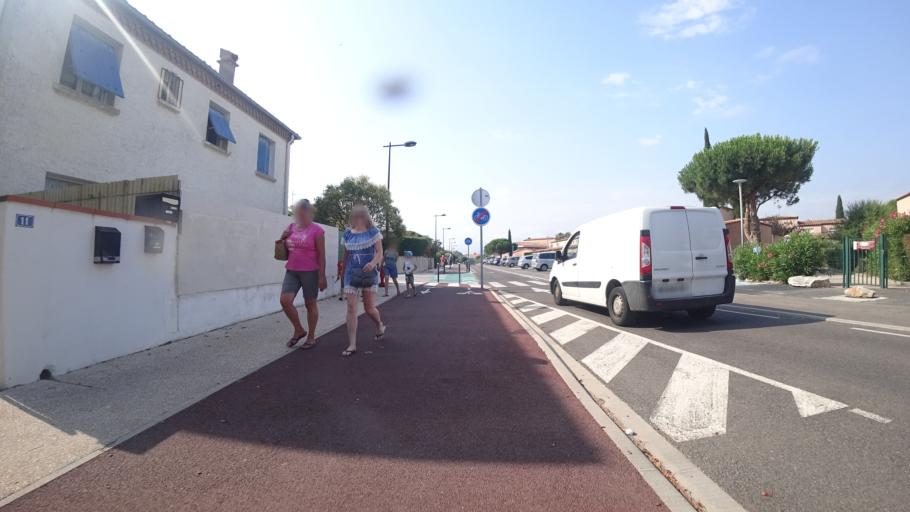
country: FR
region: Languedoc-Roussillon
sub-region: Departement des Pyrenees-Orientales
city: Saint-Cyprien-Plage
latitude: 42.6270
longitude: 3.0318
